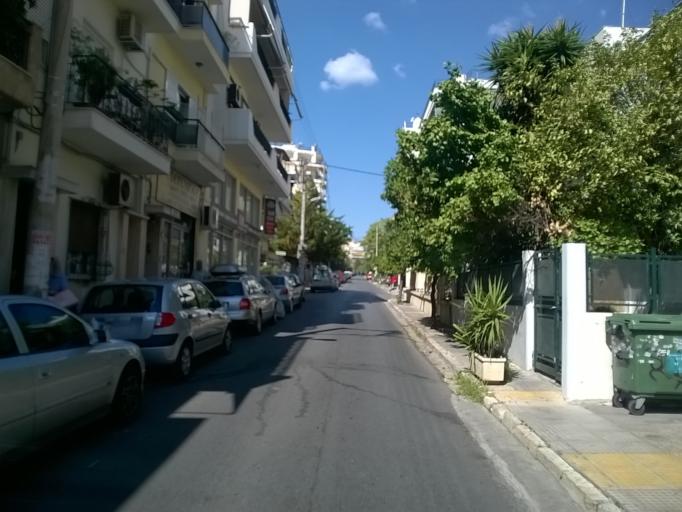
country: GR
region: Attica
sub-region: Nomos Piraios
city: Nikaia
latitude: 37.9689
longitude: 23.6552
